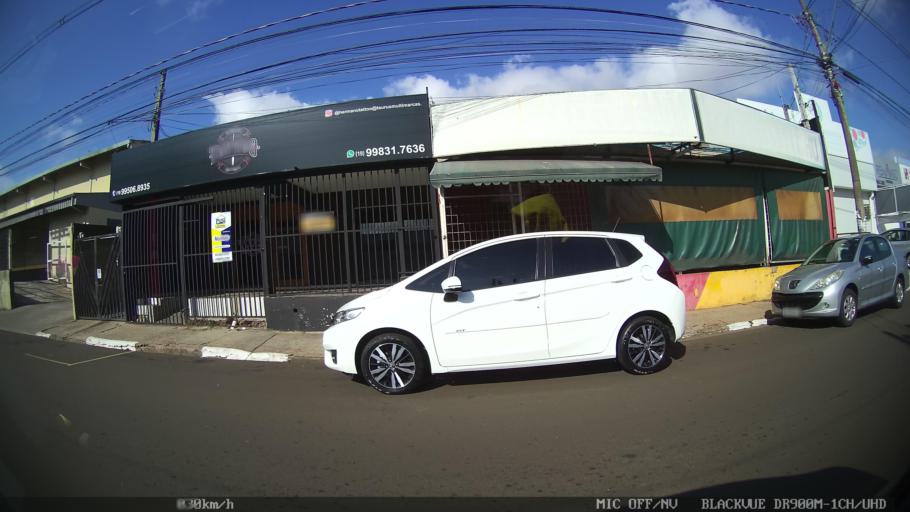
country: BR
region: Sao Paulo
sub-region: Hortolandia
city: Hortolandia
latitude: -22.8652
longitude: -47.2150
